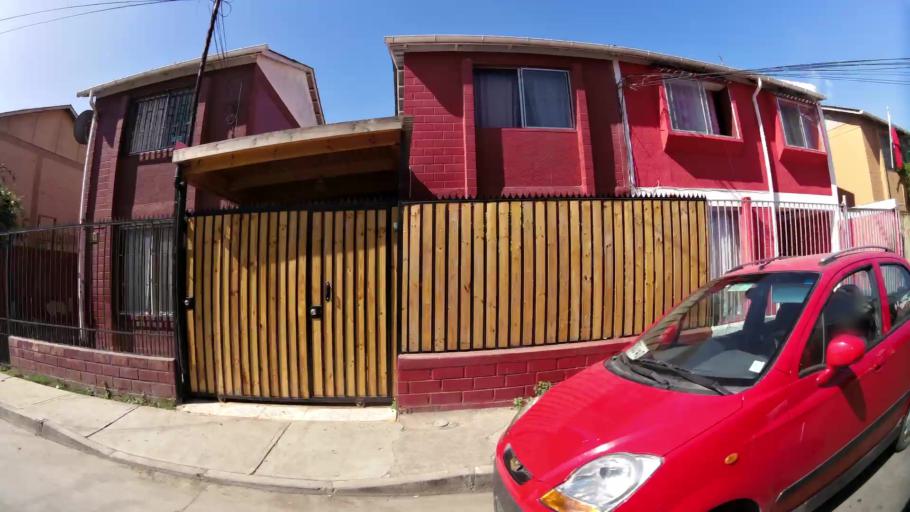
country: CL
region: Santiago Metropolitan
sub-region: Provincia de Santiago
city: Lo Prado
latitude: -33.3481
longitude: -70.7563
